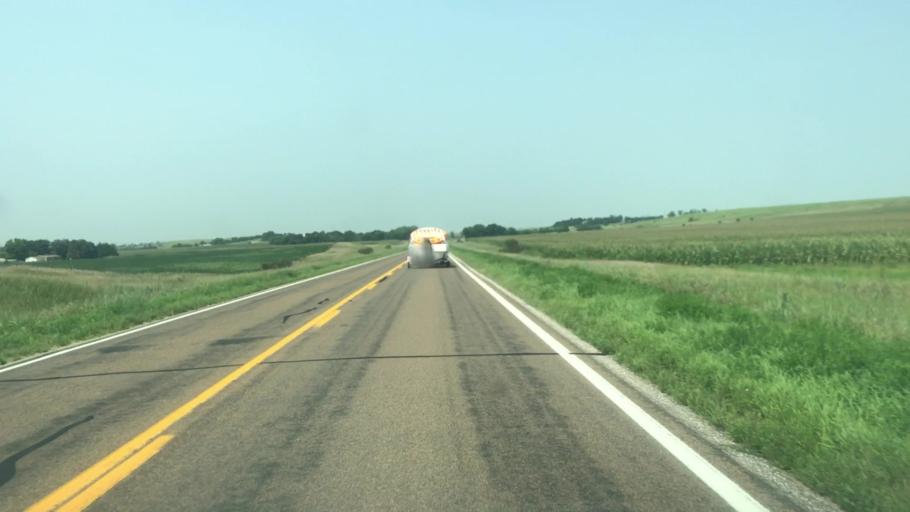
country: US
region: Nebraska
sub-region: Sherman County
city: Loup City
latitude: 41.2518
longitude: -98.9390
